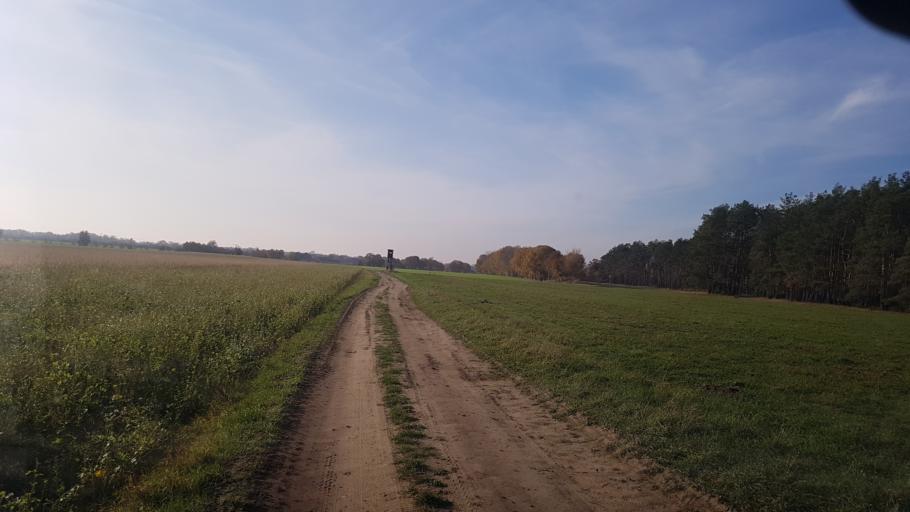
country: DE
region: Brandenburg
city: Schilda
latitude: 51.6407
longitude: 13.3365
